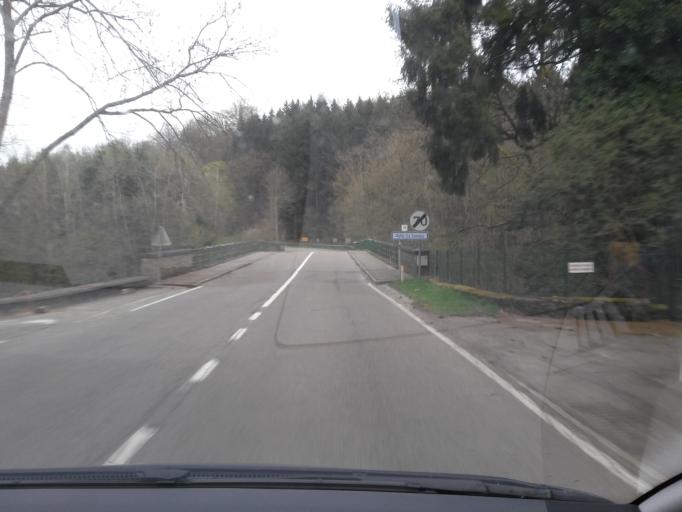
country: BE
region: Wallonia
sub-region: Province du Luxembourg
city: Herbeumont
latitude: 49.7696
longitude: 5.2362
